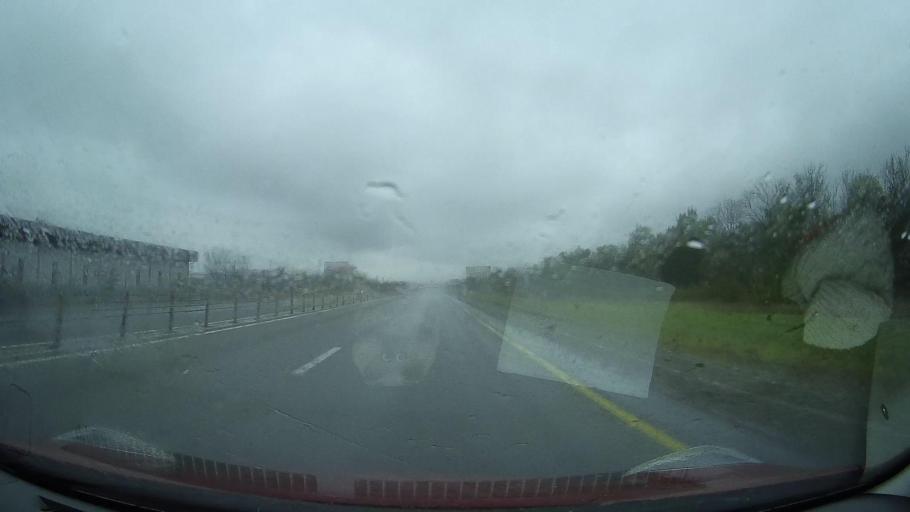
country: RU
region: Stavropol'skiy
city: Nevinnomyssk
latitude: 44.6400
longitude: 41.9728
